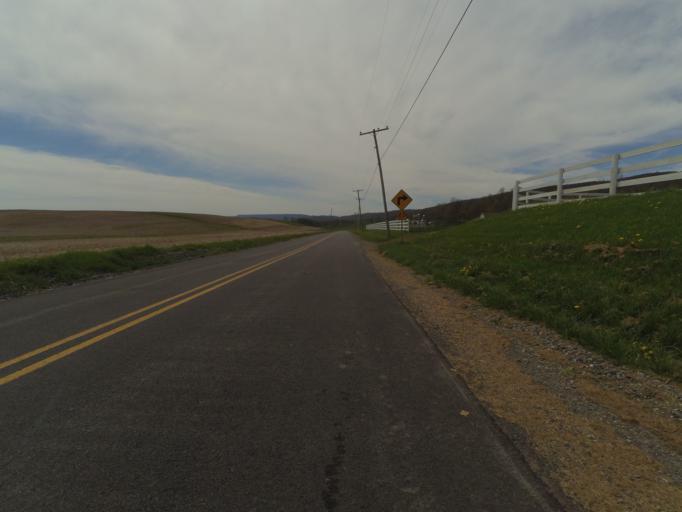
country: US
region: Pennsylvania
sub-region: Blair County
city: Tyrone
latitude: 40.7061
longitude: -78.1574
